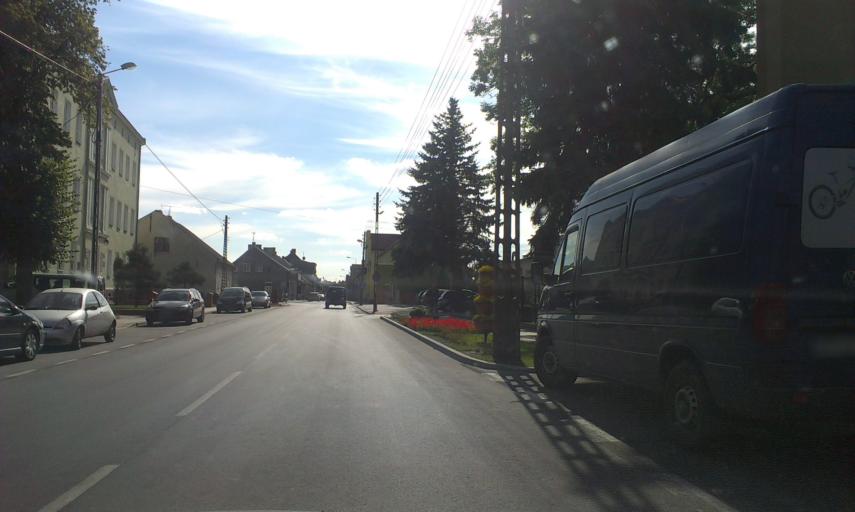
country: PL
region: Greater Poland Voivodeship
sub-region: Powiat pilski
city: Lobzenica
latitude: 53.2627
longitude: 17.2558
